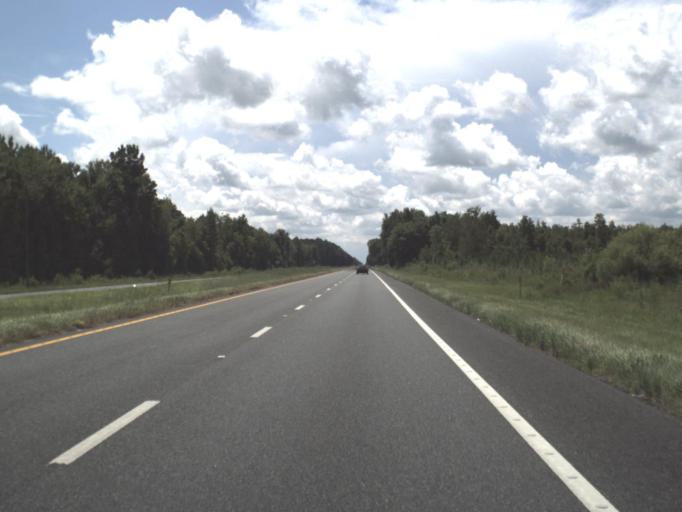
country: US
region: Florida
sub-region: Taylor County
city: Perry
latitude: 30.2662
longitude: -83.7146
